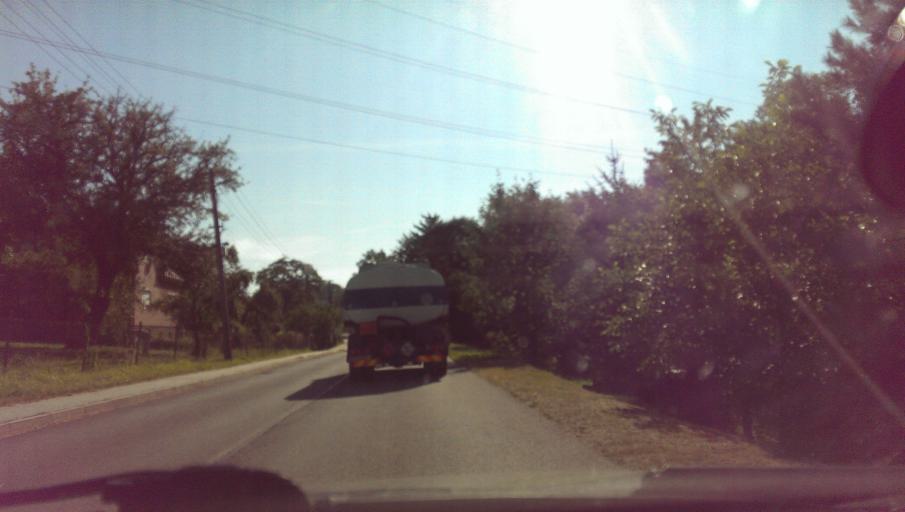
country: CZ
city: Staric
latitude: 49.6838
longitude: 18.2576
